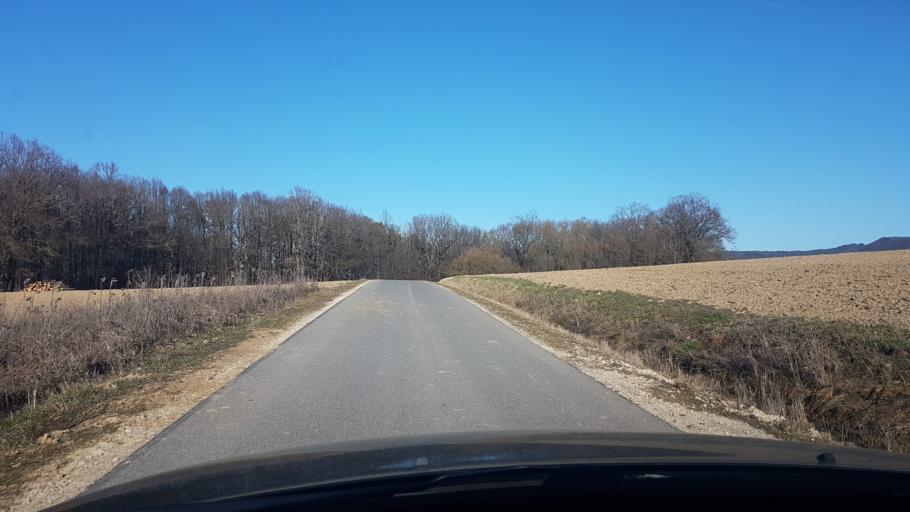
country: DE
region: Bavaria
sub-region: Upper Franconia
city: Zapfendorf
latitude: 50.0182
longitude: 10.9866
